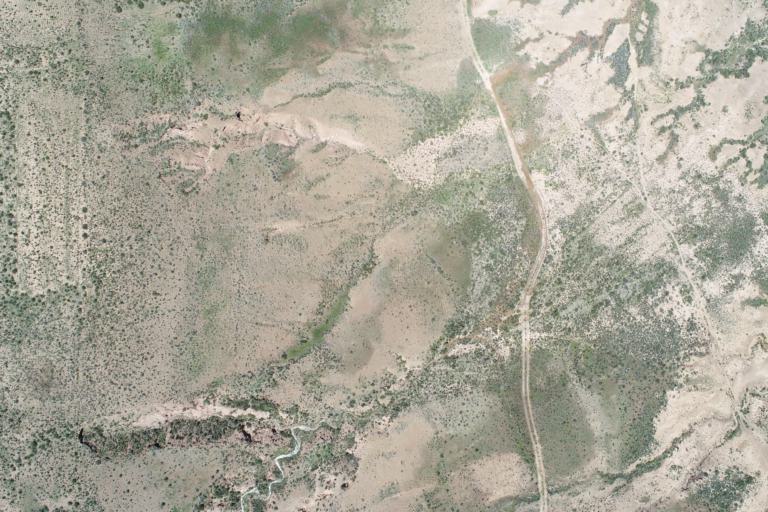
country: BO
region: La Paz
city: Curahuara de Carangas
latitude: -17.3196
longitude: -68.5057
